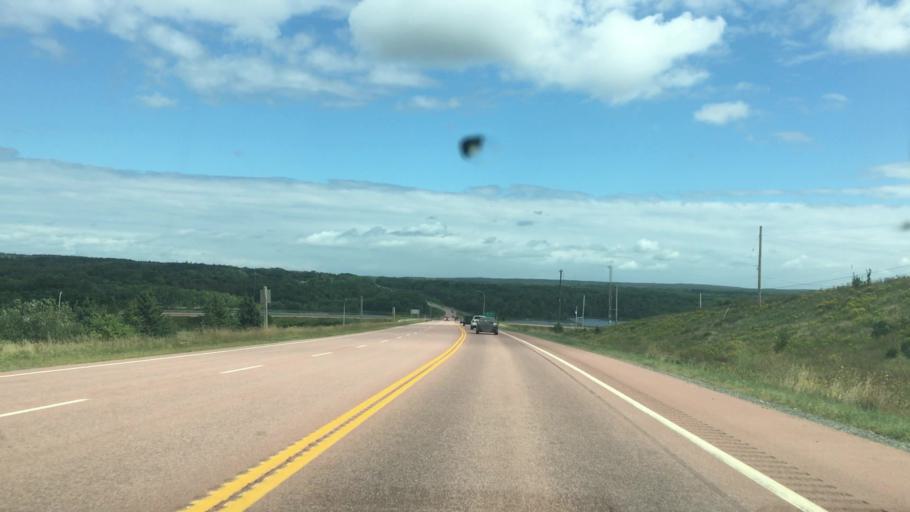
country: CA
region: Nova Scotia
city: Port Hawkesbury
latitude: 45.6128
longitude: -61.6310
